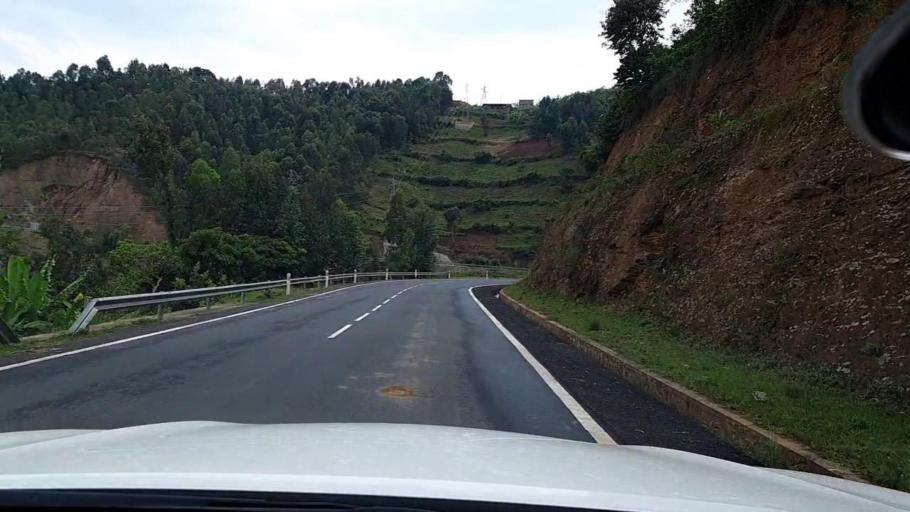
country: RW
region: Western Province
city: Kibuye
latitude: -2.1844
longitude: 29.2899
